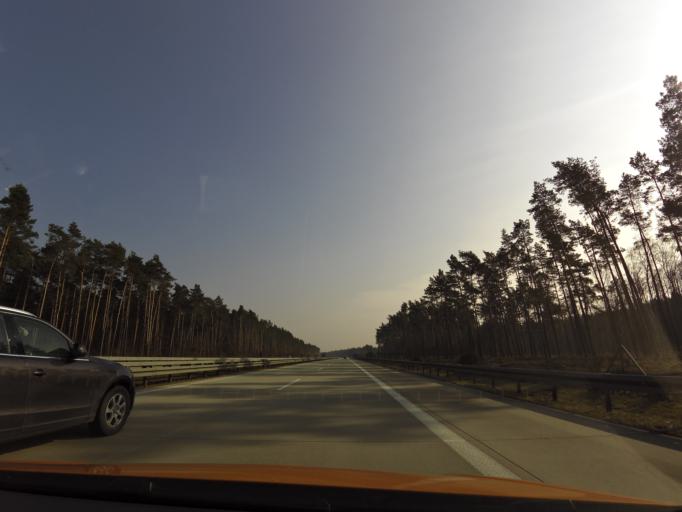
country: DE
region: Brandenburg
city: Briesen
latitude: 52.3266
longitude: 14.2785
